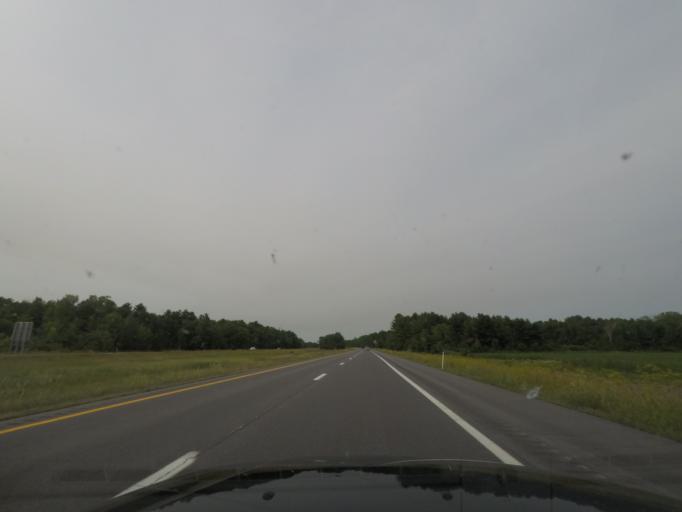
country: US
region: New York
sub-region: Clinton County
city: Cumberland Head
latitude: 44.8387
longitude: -73.4464
